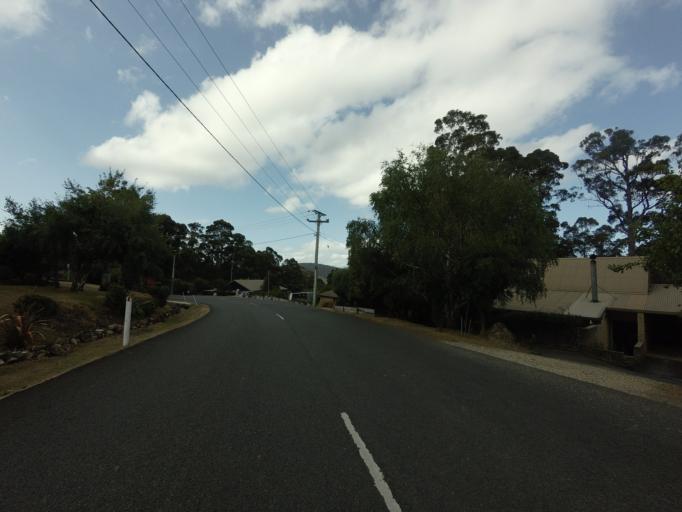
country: AU
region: Tasmania
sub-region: Hobart
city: Dynnyrne
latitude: -42.9037
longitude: 147.2707
